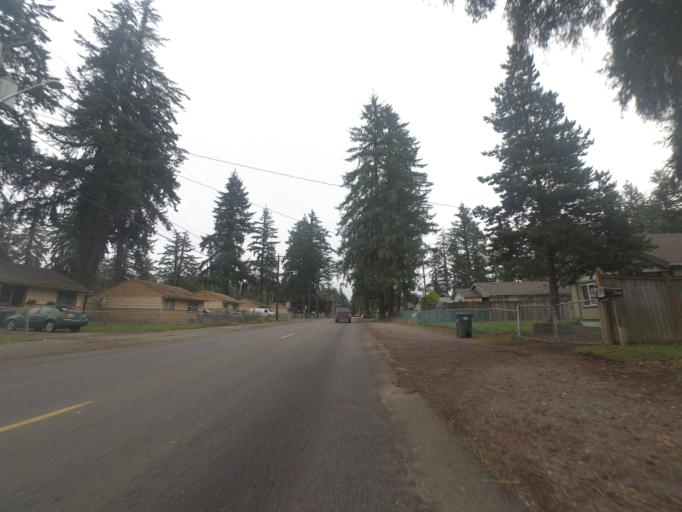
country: US
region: Washington
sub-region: Pierce County
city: McChord Air Force Base
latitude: 47.1212
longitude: -122.5282
